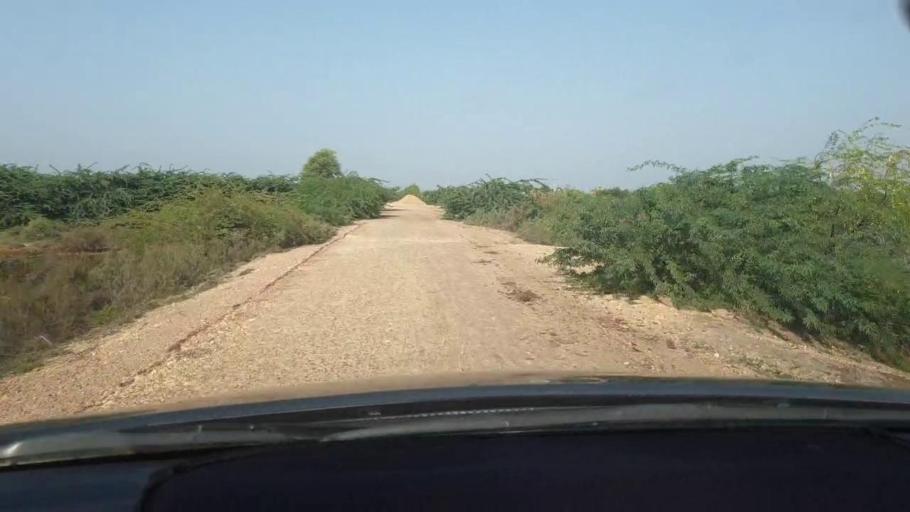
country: PK
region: Sindh
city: Tando Bago
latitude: 24.6800
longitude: 69.1357
